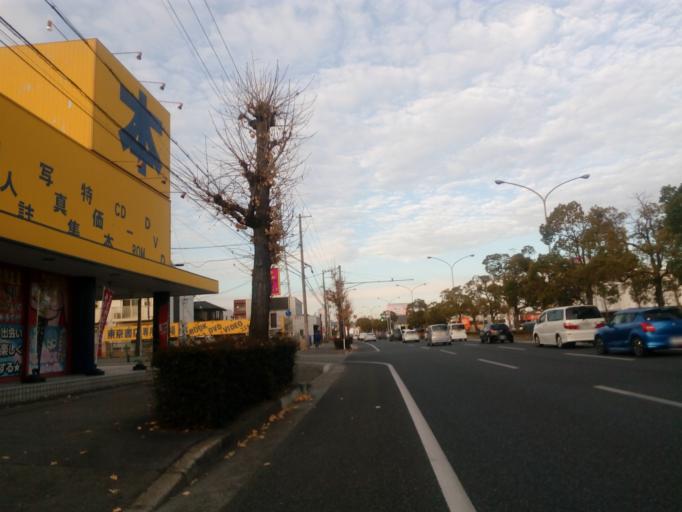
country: JP
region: Hyogo
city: Himeji
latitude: 34.8016
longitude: 134.6794
